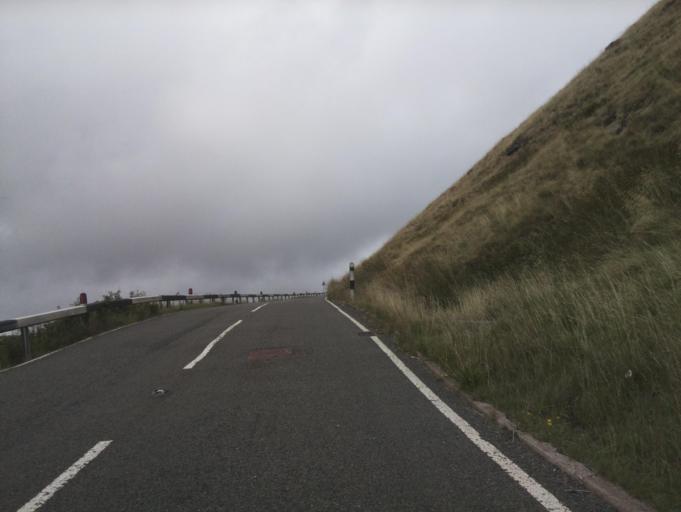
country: GB
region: England
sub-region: Kirklees
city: Meltham
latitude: 53.5263
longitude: -1.8566
